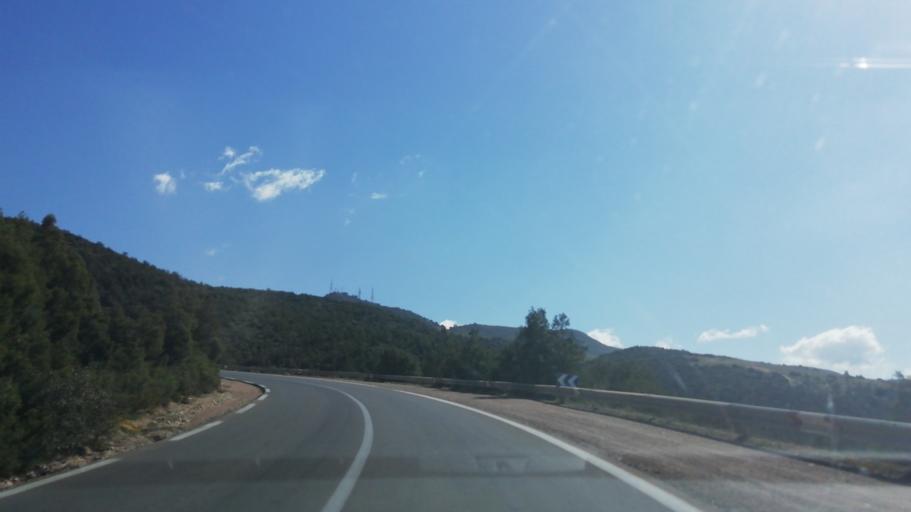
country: DZ
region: Mascara
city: Mascara
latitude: 35.4868
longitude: 0.1453
